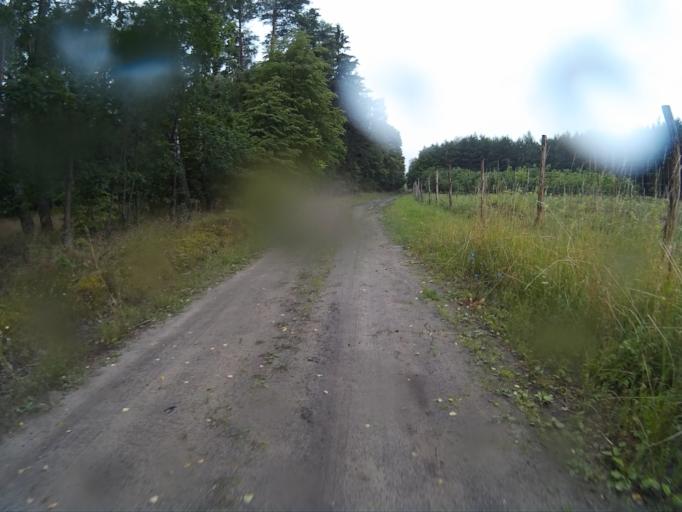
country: PL
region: Kujawsko-Pomorskie
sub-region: Powiat tucholski
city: Gostycyn
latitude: 53.5201
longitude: 17.8674
